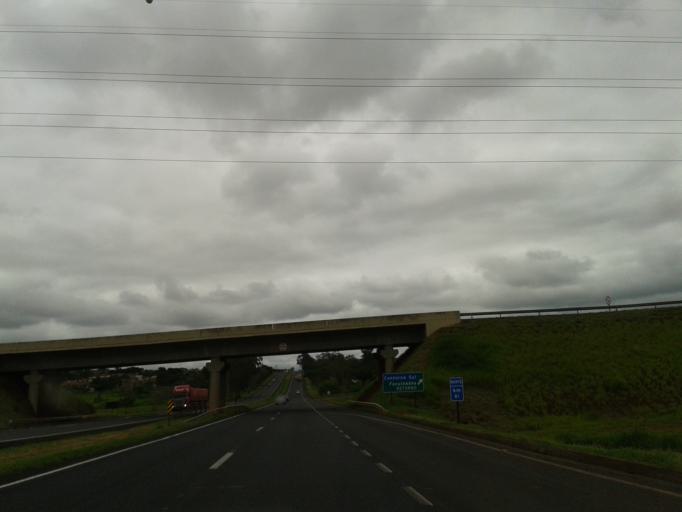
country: BR
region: Minas Gerais
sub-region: Uberlandia
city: Uberlandia
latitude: -18.9717
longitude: -48.2142
